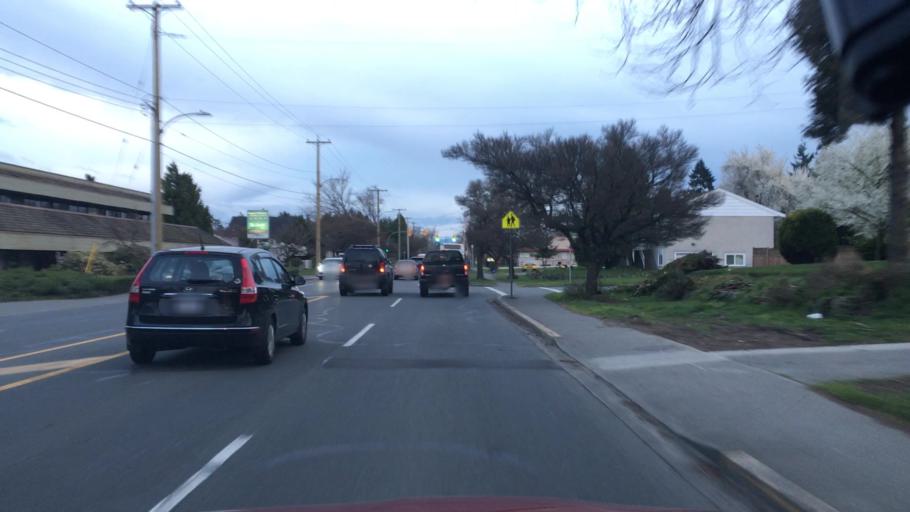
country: CA
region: British Columbia
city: Oak Bay
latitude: 48.4577
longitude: -123.3332
